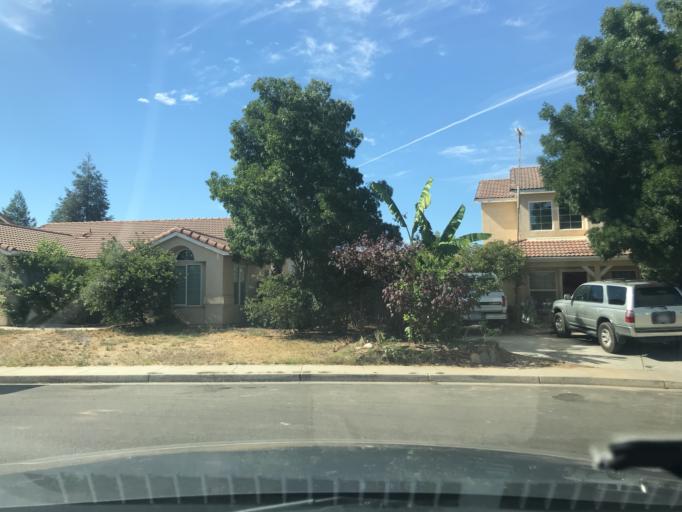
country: US
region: California
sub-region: Merced County
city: Merced
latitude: 37.3254
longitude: -120.5259
